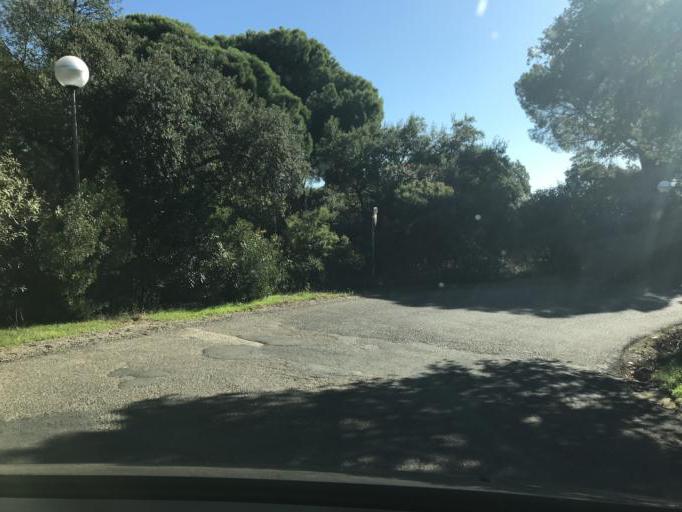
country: ES
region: Andalusia
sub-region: Province of Cordoba
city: Cordoba
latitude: 37.9333
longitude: -4.8033
